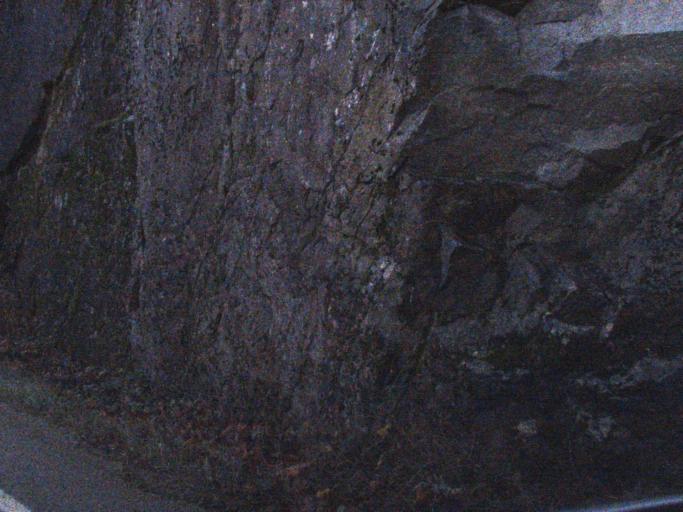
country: US
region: Washington
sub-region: Snohomish County
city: Darrington
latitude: 48.6319
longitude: -121.3252
